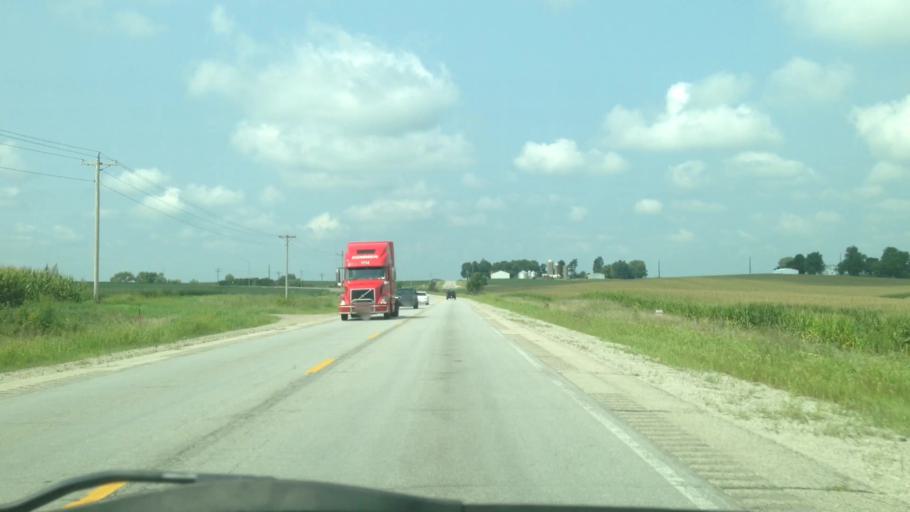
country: US
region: Iowa
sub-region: Benton County
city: Walford
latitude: 41.8762
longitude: -91.8617
